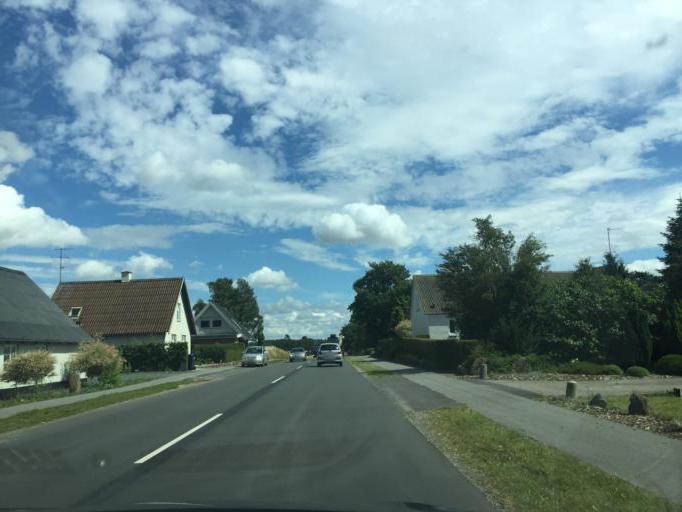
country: DK
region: South Denmark
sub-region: Nordfyns Kommune
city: Otterup
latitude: 55.5224
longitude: 10.3601
